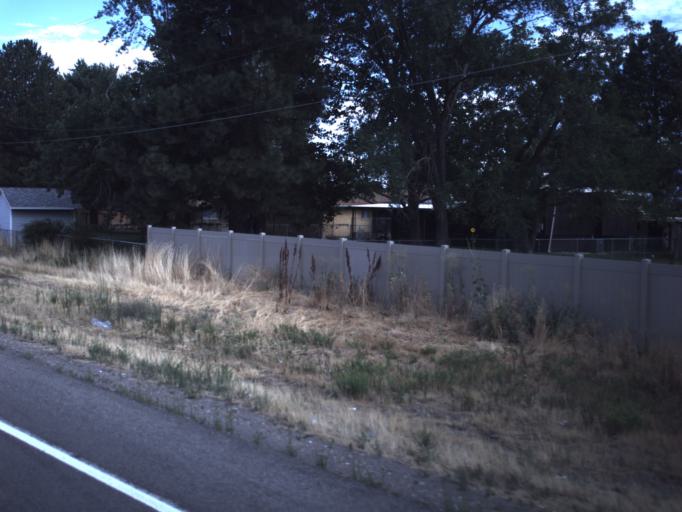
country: US
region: Utah
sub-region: Weber County
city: Washington Terrace
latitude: 41.1658
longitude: -111.9579
